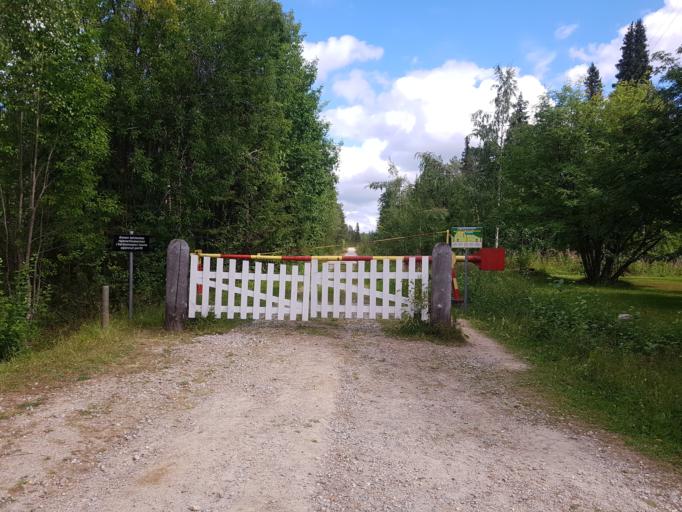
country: FI
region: Kainuu
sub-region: Kehys-Kainuu
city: Kuhmo
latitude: 64.8084
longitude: 29.6795
